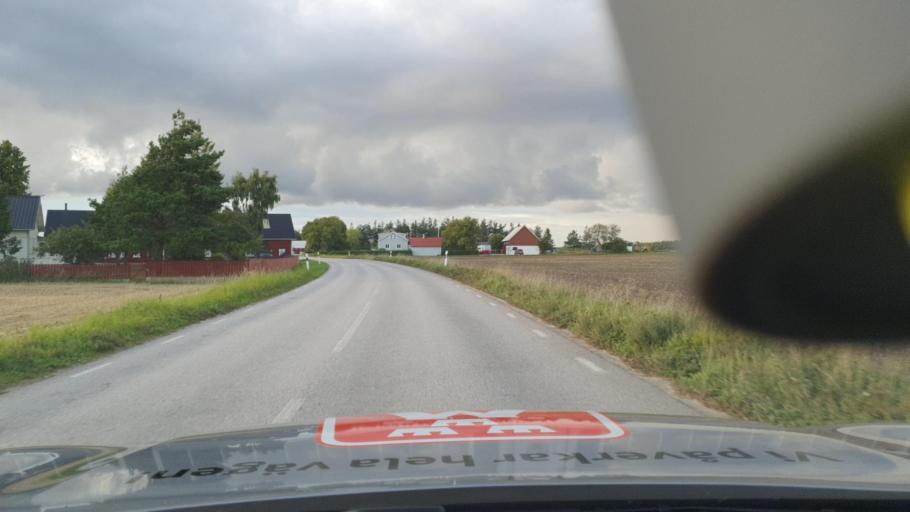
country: SE
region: Gotland
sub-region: Gotland
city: Vibble
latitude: 57.5055
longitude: 18.3705
